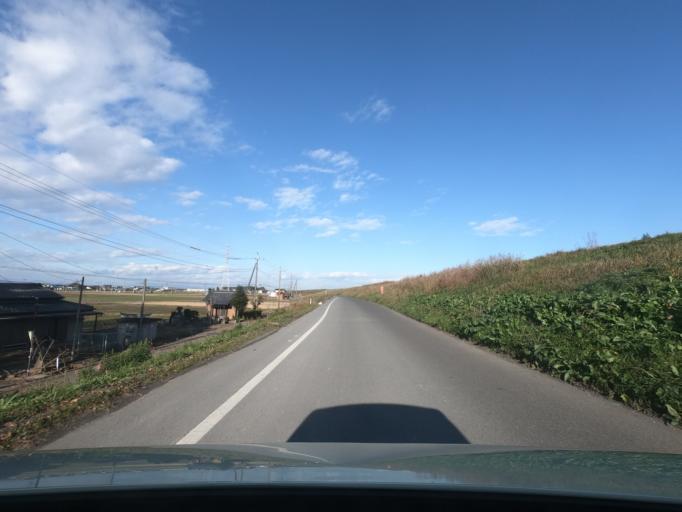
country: JP
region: Ibaraki
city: Koga
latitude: 36.2492
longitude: 139.7341
